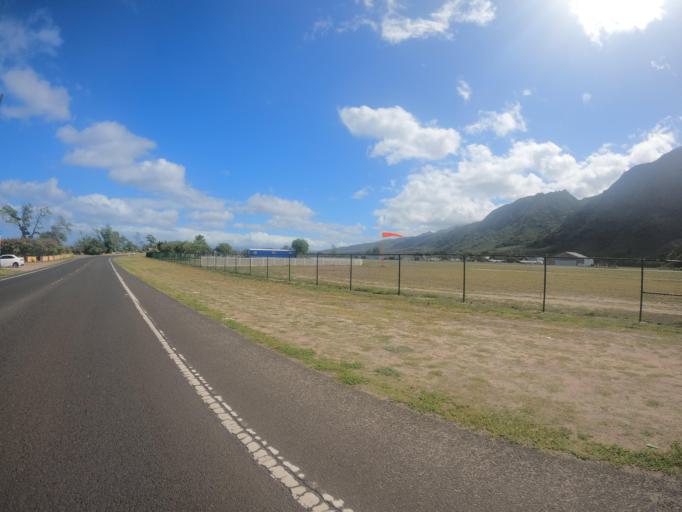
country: US
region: Hawaii
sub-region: Honolulu County
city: Mokuleia
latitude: 21.5802
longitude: -158.2099
